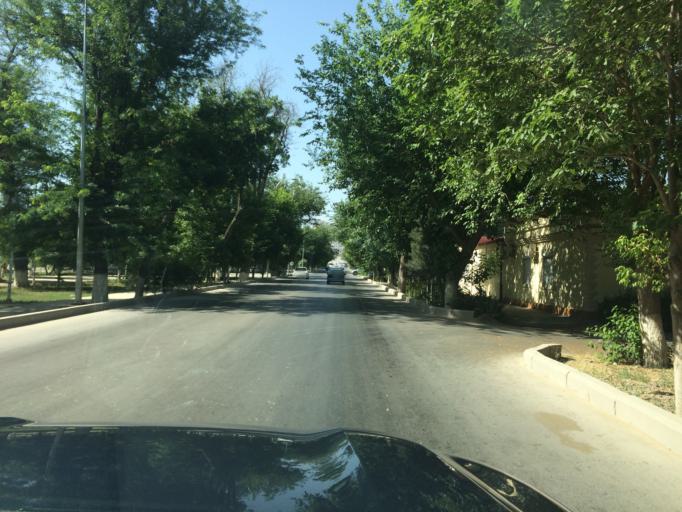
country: TM
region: Ahal
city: Ashgabat
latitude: 37.9481
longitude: 58.3612
